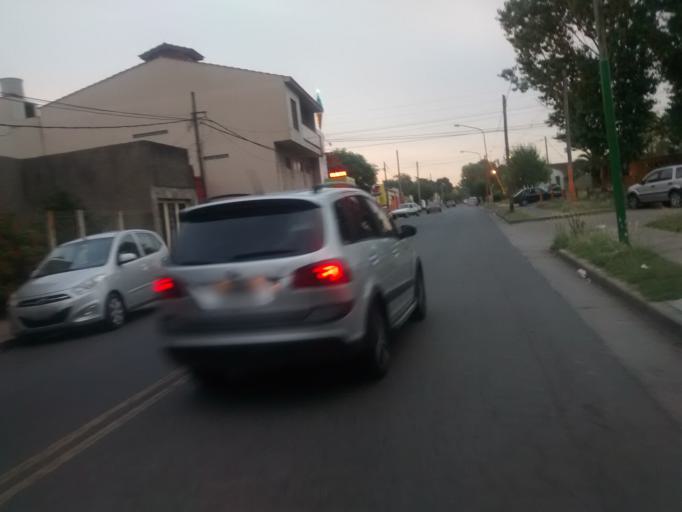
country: AR
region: Buenos Aires
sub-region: Partido de La Plata
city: La Plata
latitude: -34.9428
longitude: -57.9249
